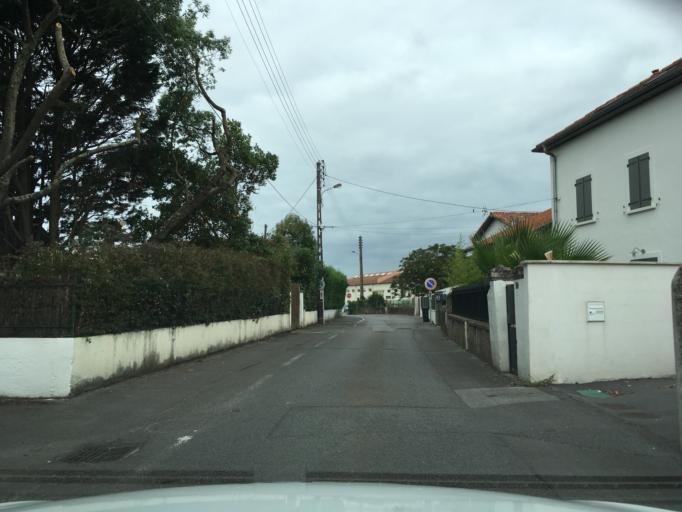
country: FR
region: Aquitaine
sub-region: Departement des Pyrenees-Atlantiques
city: Bayonne
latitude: 43.4990
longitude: -1.5005
